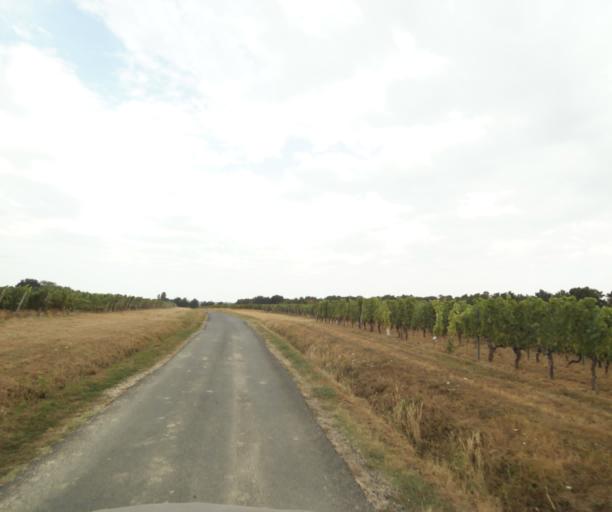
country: FR
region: Aquitaine
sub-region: Departement de la Gironde
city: Creon
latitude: 44.7519
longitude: -0.3408
